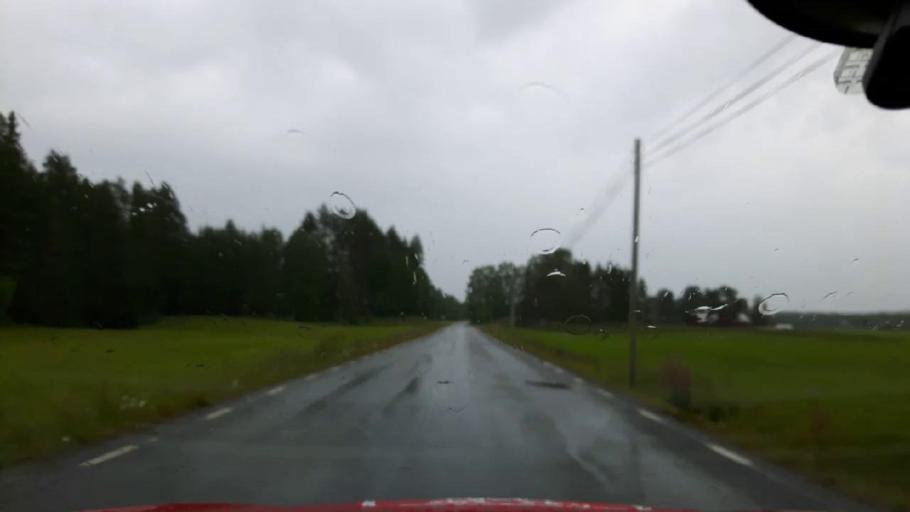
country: SE
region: Jaemtland
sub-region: OEstersunds Kommun
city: Brunflo
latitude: 62.9961
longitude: 14.7763
